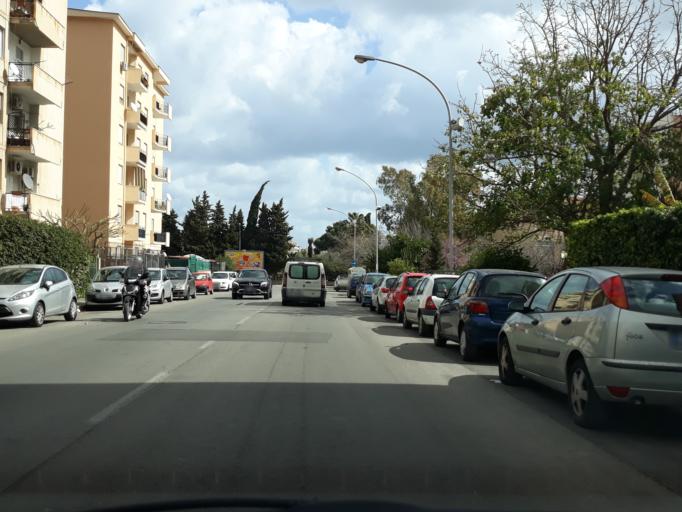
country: IT
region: Sicily
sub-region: Palermo
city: Palermo
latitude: 38.1164
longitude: 13.3375
